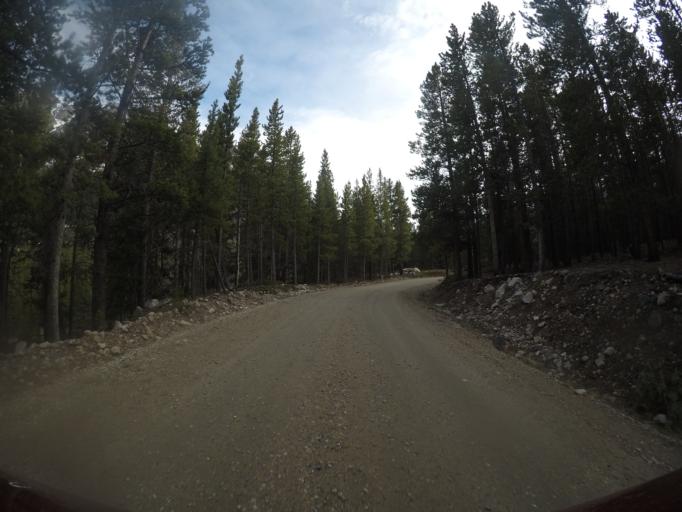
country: US
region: Montana
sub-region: Carbon County
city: Red Lodge
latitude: 45.0264
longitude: -109.4420
